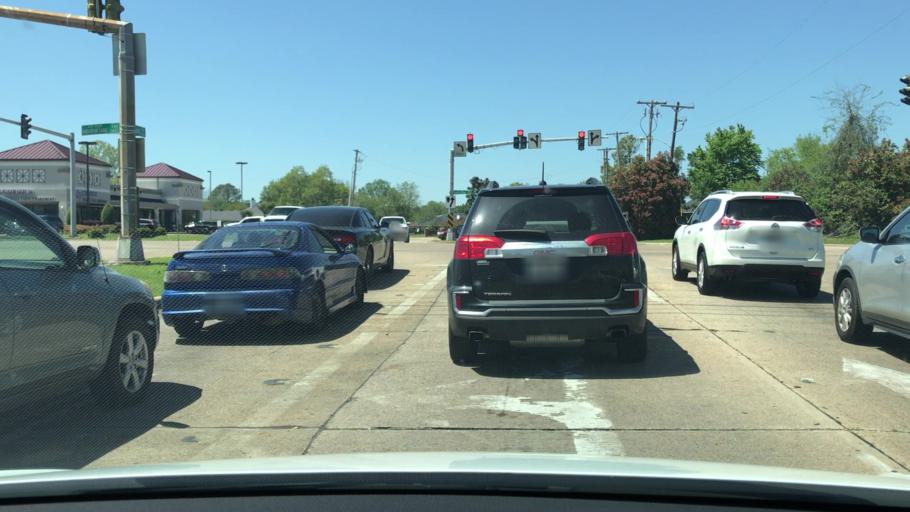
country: US
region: Louisiana
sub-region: Bossier Parish
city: Bossier City
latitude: 32.4274
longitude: -93.7174
